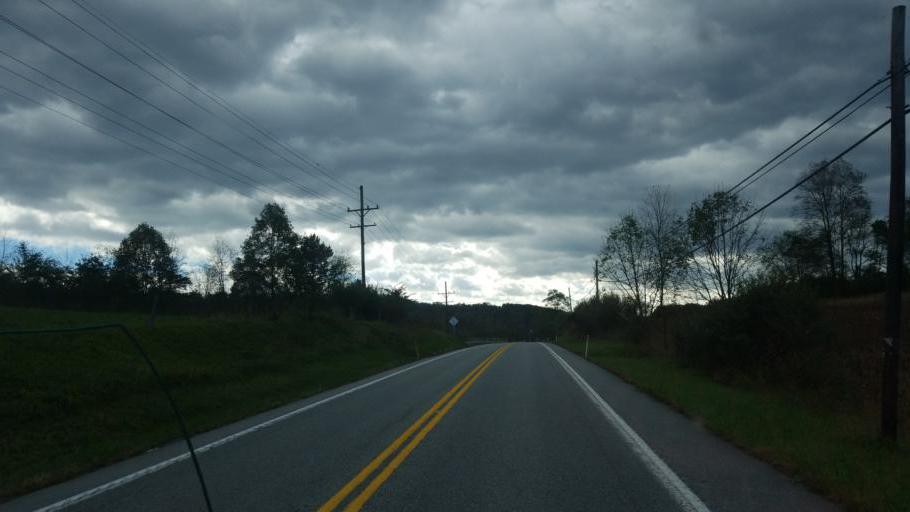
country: US
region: Pennsylvania
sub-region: Fulton County
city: McConnellsburg
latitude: 39.9530
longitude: -78.0241
